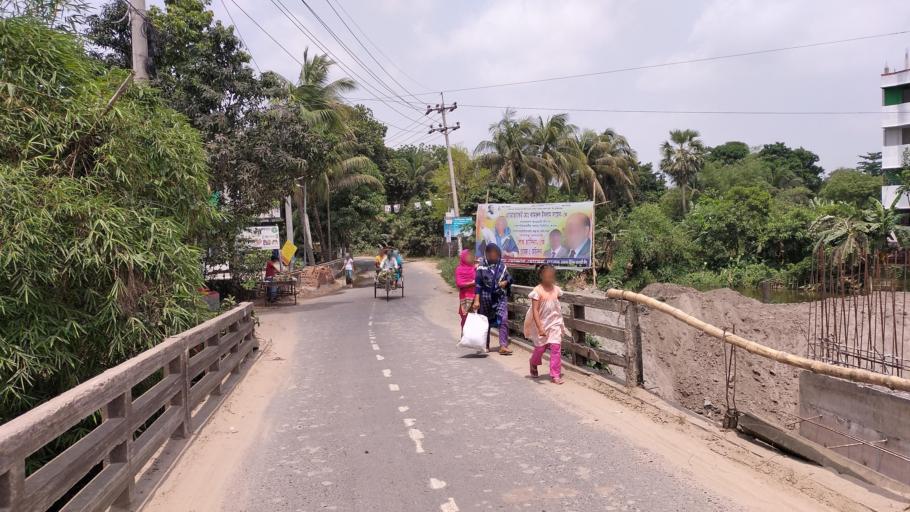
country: BD
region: Dhaka
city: Azimpur
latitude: 23.7316
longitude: 90.3139
